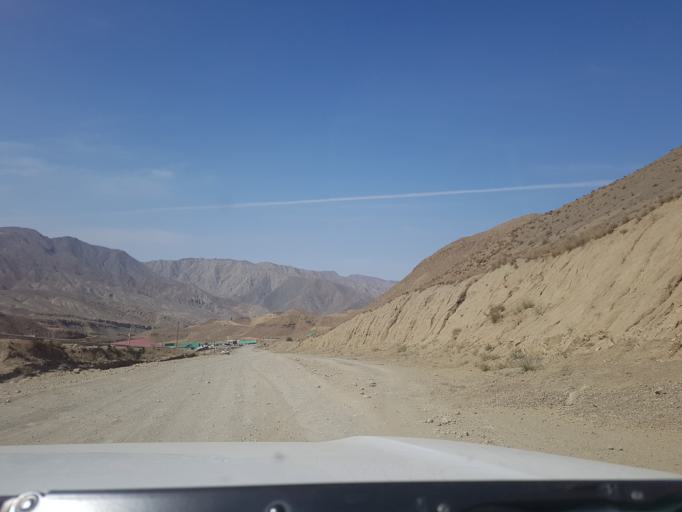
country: TM
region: Ahal
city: Baharly
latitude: 38.4495
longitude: 57.0474
